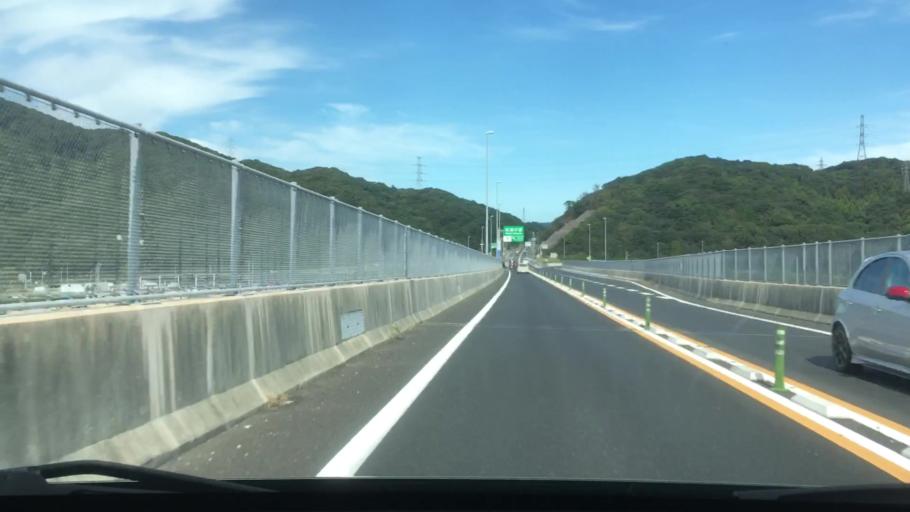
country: JP
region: Nagasaki
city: Sasebo
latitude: 33.1997
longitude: 129.6752
